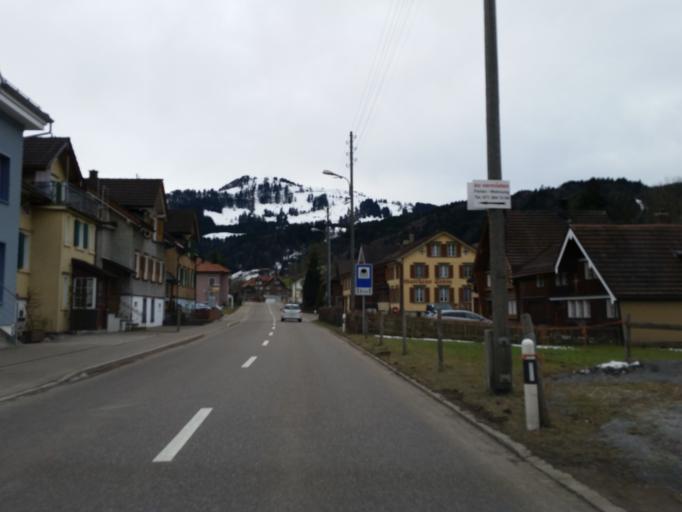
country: CH
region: Appenzell Ausserrhoden
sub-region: Bezirk Hinterland
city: Urnasch
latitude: 47.3070
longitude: 9.2757
